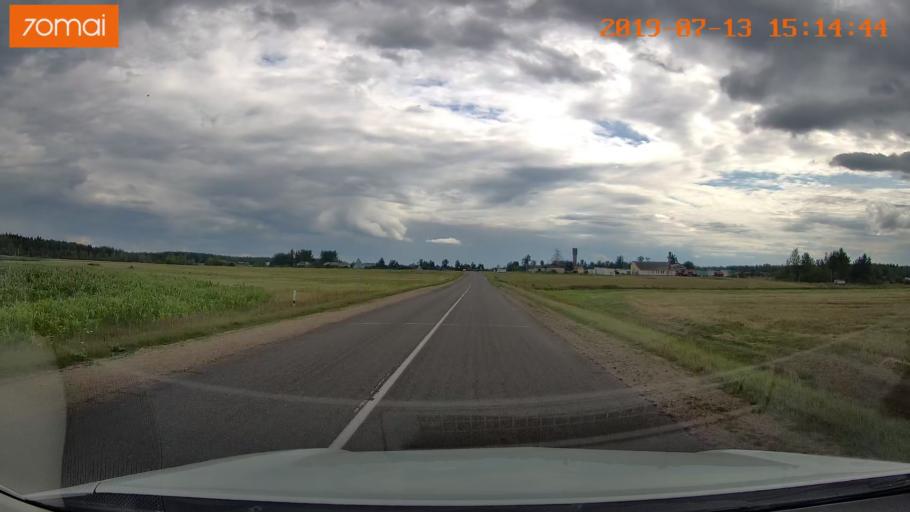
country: BY
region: Mogilev
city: Hlusha
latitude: 53.1235
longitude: 28.8215
